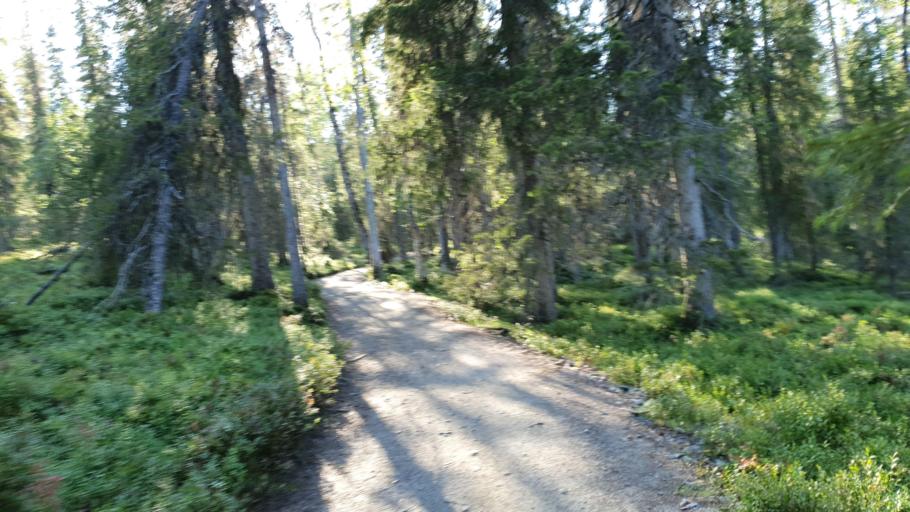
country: FI
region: Lapland
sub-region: Tunturi-Lappi
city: Kolari
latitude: 67.5983
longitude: 24.2121
